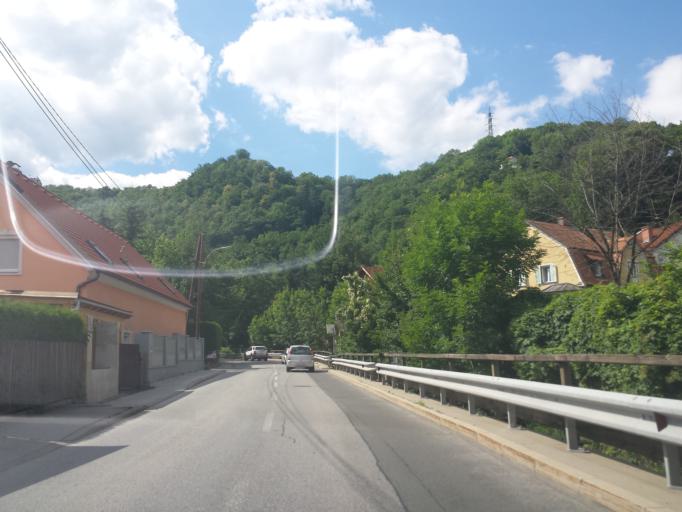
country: AT
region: Styria
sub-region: Graz Stadt
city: Goesting
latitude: 47.1003
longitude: 15.3907
